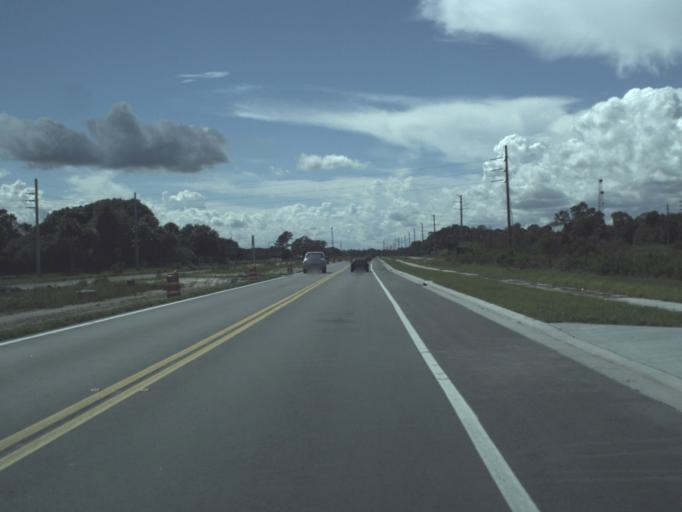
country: US
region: Florida
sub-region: Okeechobee County
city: Cypress Quarters
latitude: 27.2521
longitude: -80.7775
